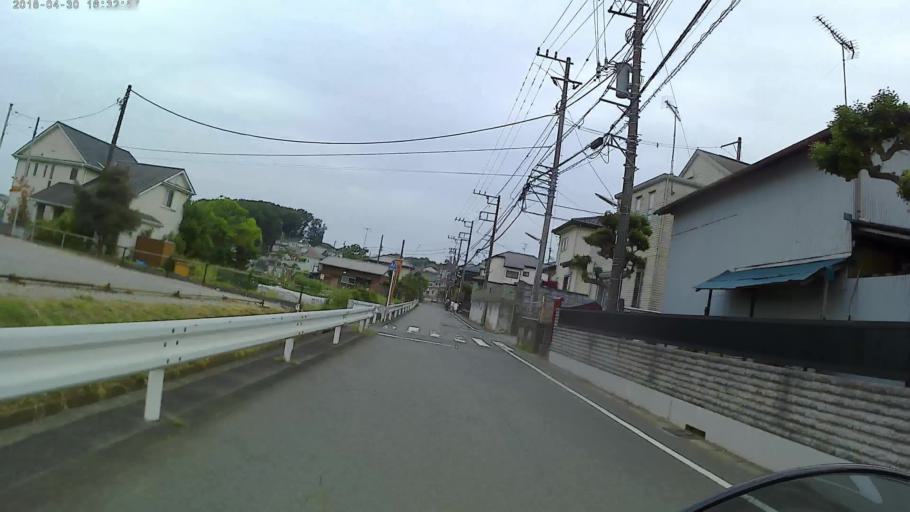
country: JP
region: Kanagawa
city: Zama
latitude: 35.4518
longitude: 139.4024
